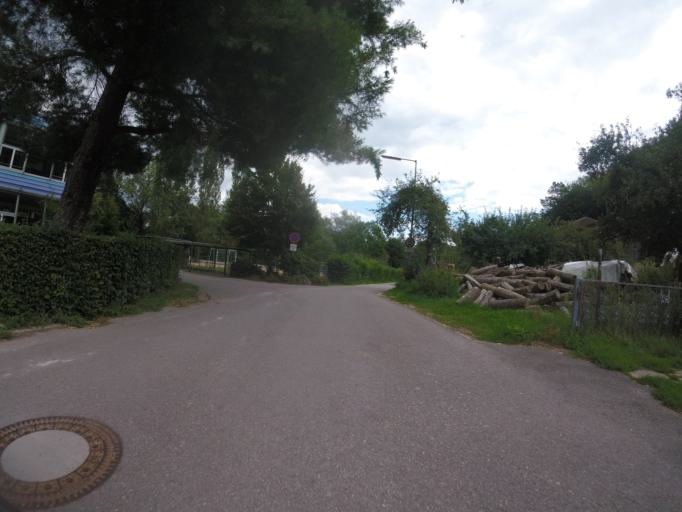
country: DE
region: Baden-Wuerttemberg
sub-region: Regierungsbezirk Stuttgart
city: Lorch
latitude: 48.7955
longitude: 9.6930
